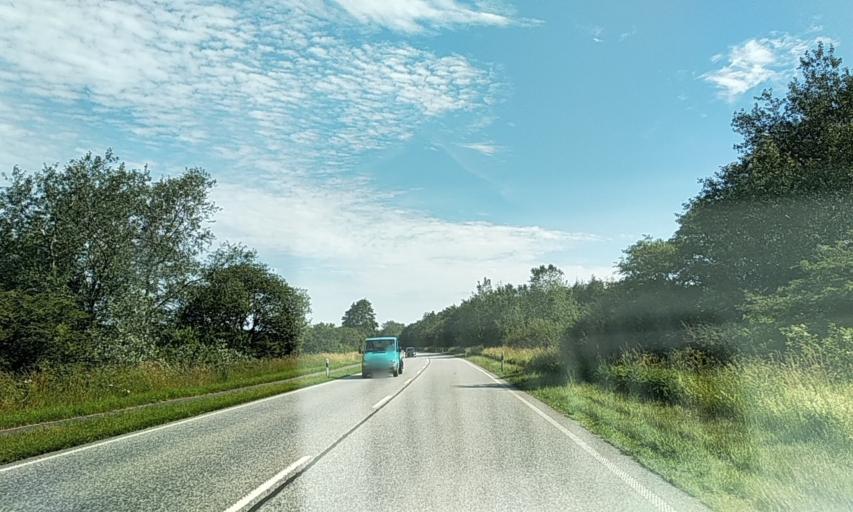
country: DE
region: Schleswig-Holstein
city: Jagel
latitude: 54.4423
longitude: 9.5359
